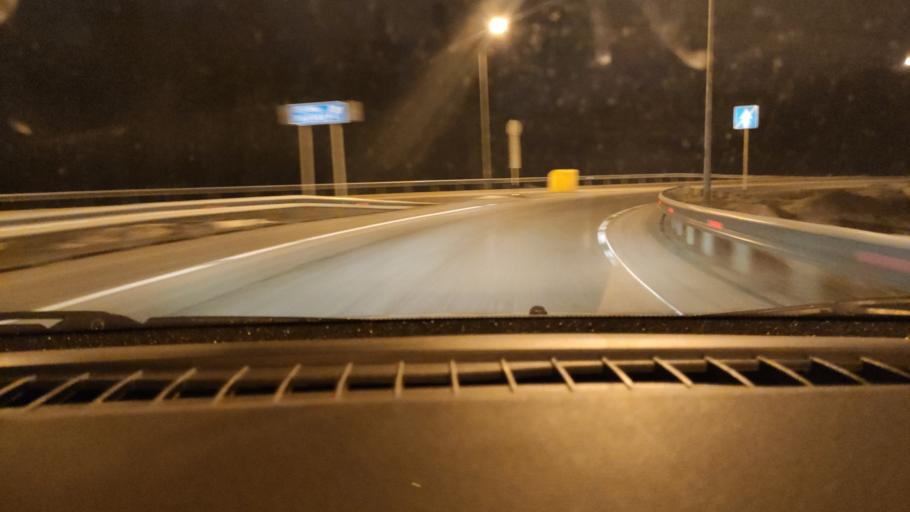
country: RU
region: Perm
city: Ferma
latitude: 57.9501
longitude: 56.3861
